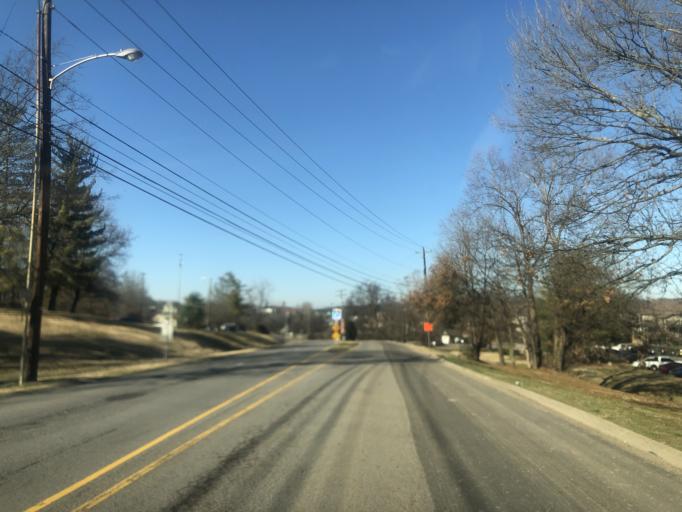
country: US
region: Tennessee
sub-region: Rutherford County
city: La Vergne
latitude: 36.0400
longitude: -86.6601
